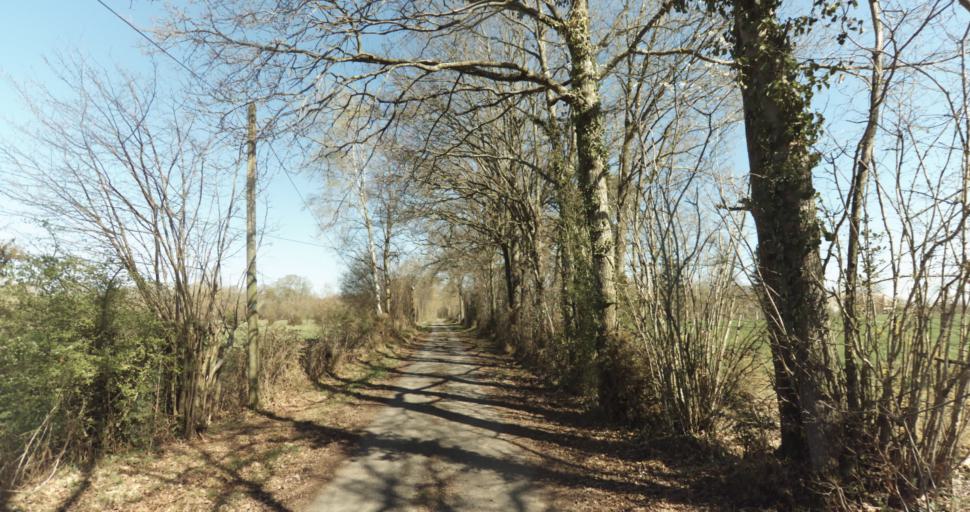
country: FR
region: Lower Normandy
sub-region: Departement du Calvados
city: Saint-Pierre-sur-Dives
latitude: 48.9942
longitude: 0.0525
